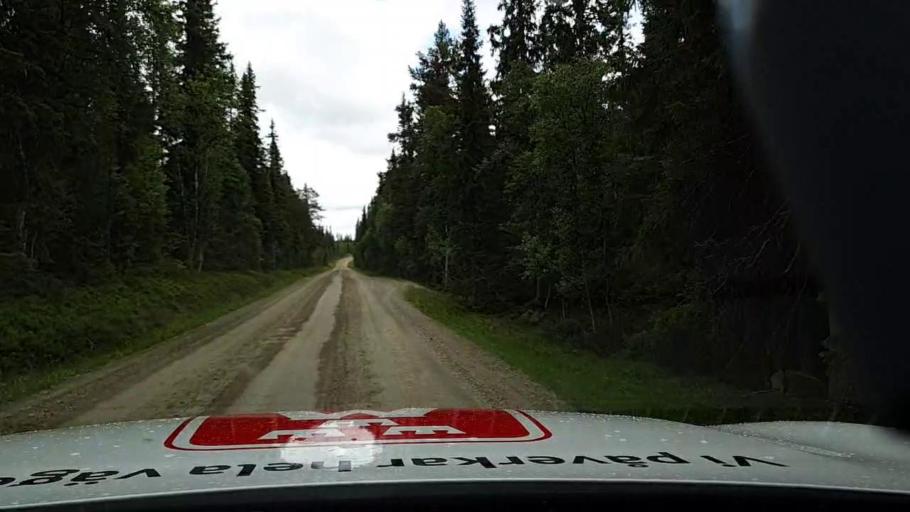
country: SE
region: Jaemtland
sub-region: Are Kommun
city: Jarpen
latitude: 62.6019
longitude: 13.2294
